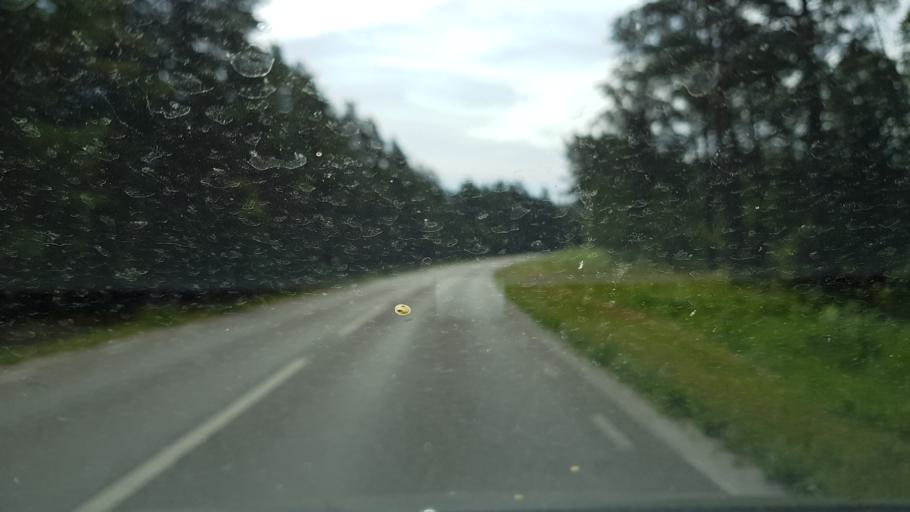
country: SE
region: Gotland
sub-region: Gotland
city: Hemse
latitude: 57.4689
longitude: 18.5615
